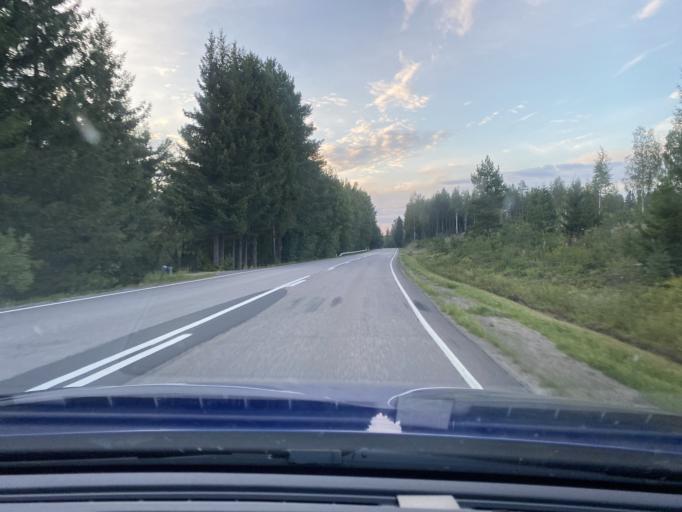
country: FI
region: Satakunta
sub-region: Pohjois-Satakunta
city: Honkajoki
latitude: 61.9341
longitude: 22.2401
